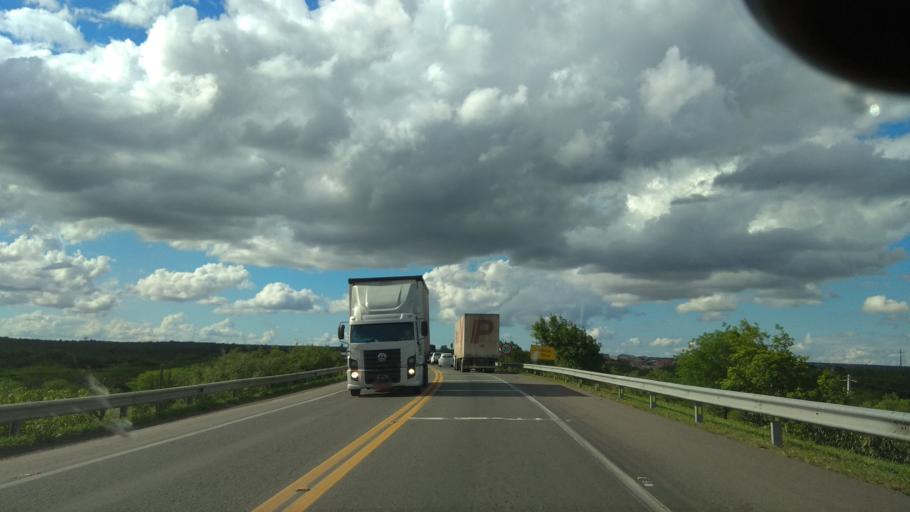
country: BR
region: Bahia
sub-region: Castro Alves
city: Castro Alves
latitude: -12.5901
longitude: -39.5246
